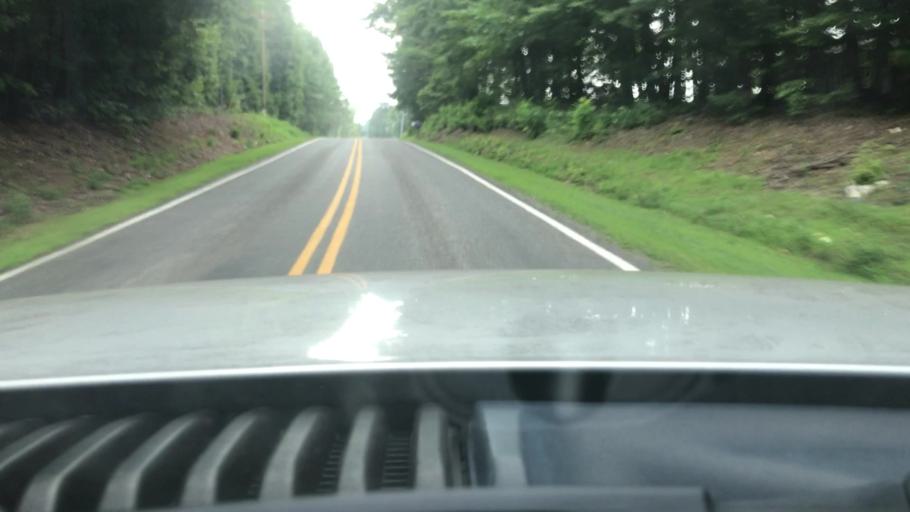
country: US
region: North Carolina
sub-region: Surry County
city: Dobson
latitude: 36.4088
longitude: -80.8155
